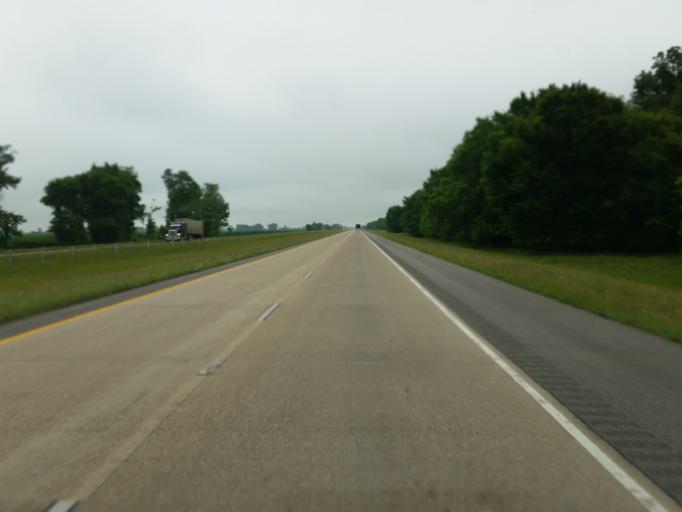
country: US
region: Louisiana
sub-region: Madison Parish
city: Tallulah
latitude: 32.3342
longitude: -91.0516
